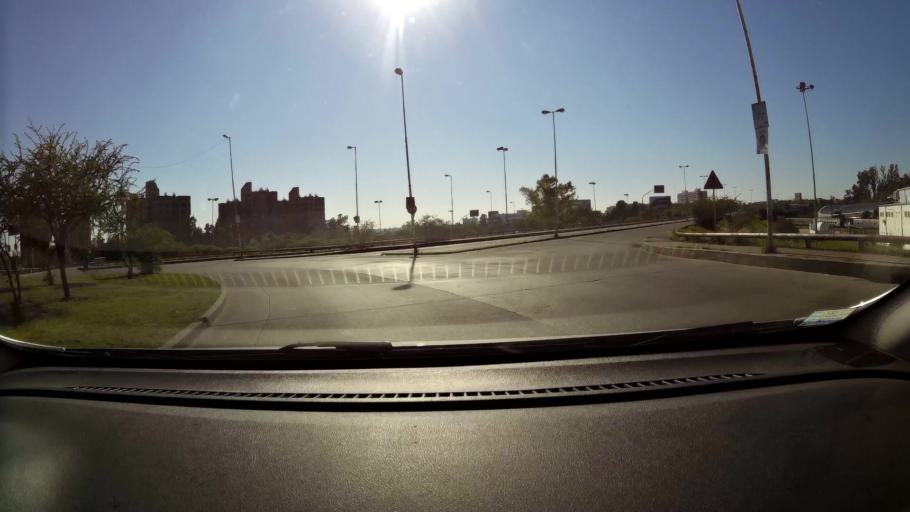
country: AR
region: Cordoba
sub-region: Departamento de Capital
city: Cordoba
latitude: -31.4229
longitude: -64.1726
